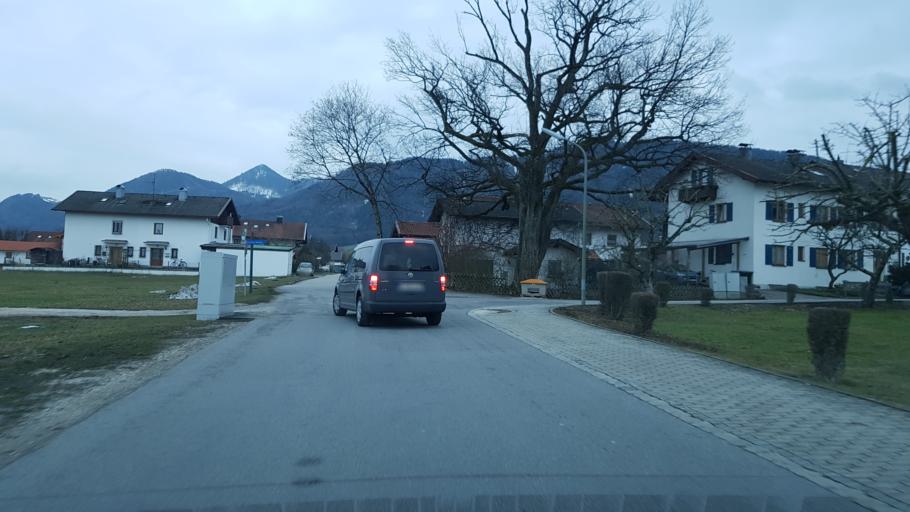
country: DE
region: Bavaria
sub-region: Upper Bavaria
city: Bernau am Chiemsee
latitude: 47.8108
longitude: 12.3791
